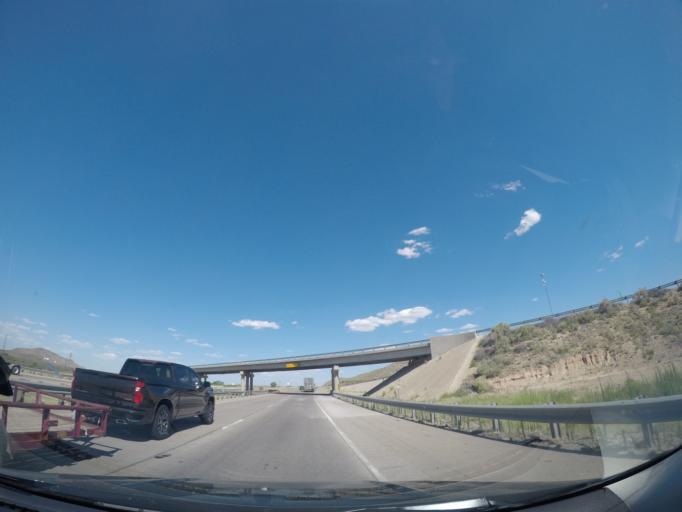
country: US
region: Texas
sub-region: Hudspeth County
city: Sierra Blanca
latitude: 31.1792
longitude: -105.3779
